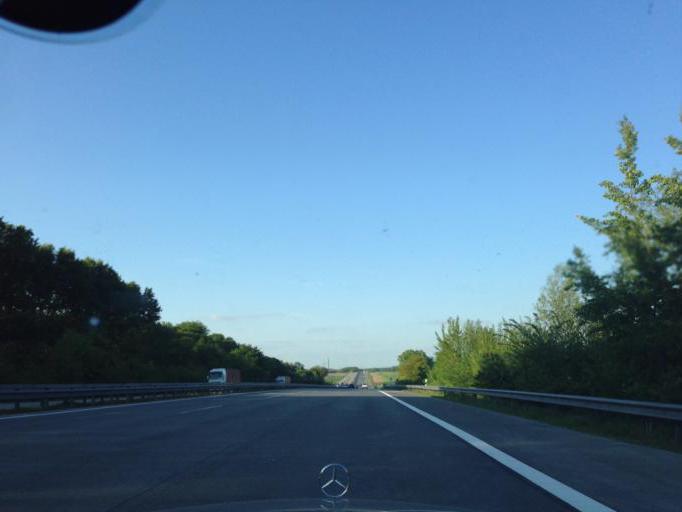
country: DE
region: Schleswig-Holstein
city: Lasbek
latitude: 53.7506
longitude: 10.3680
